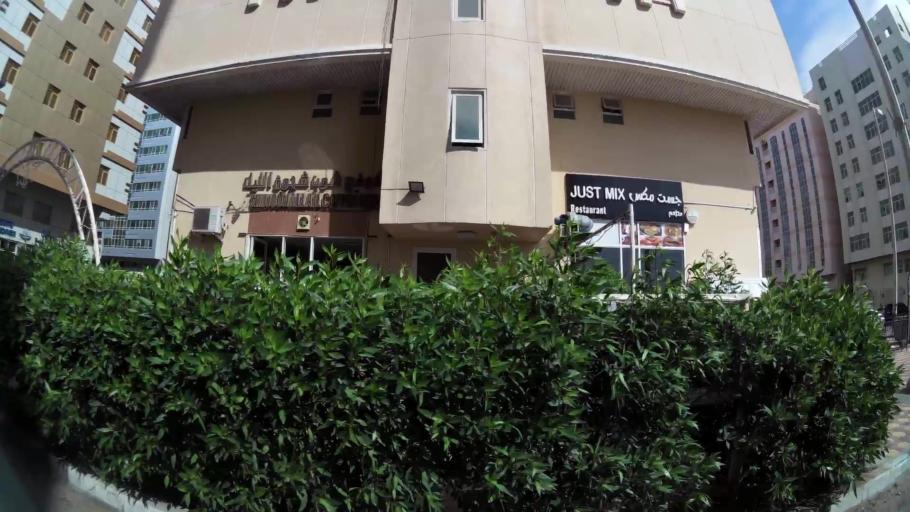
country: AE
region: Abu Dhabi
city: Abu Dhabi
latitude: 24.3359
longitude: 54.5305
